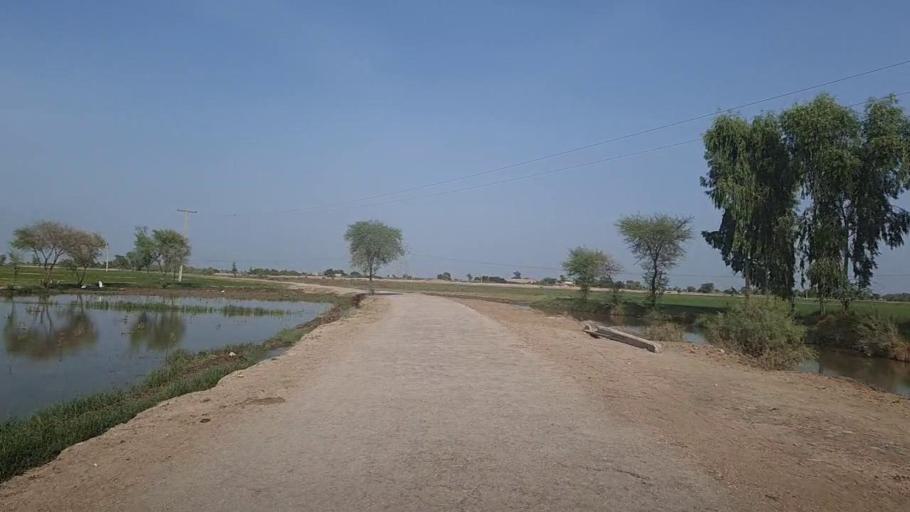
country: PK
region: Sindh
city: Sita Road
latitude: 27.0900
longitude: 67.8522
